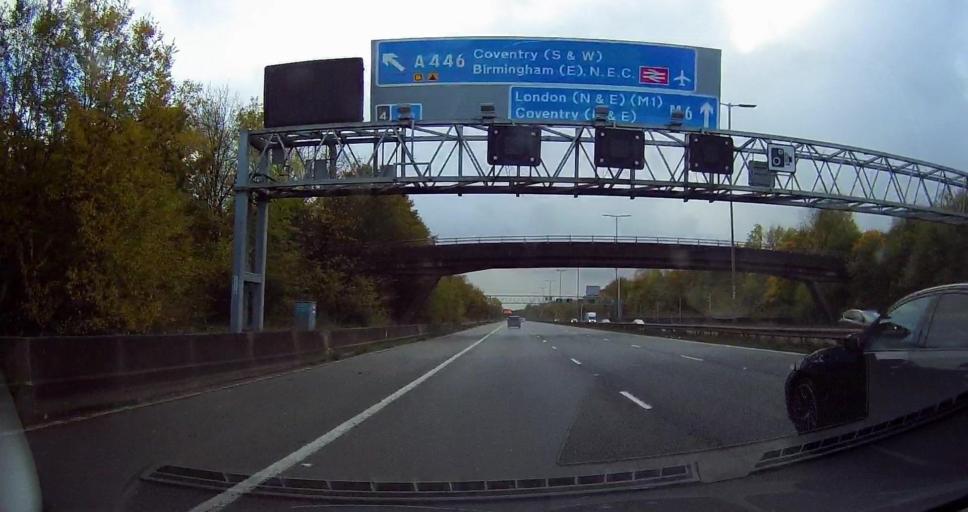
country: GB
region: England
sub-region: Warwickshire
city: Water Orton
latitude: 52.4988
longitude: -1.7377
